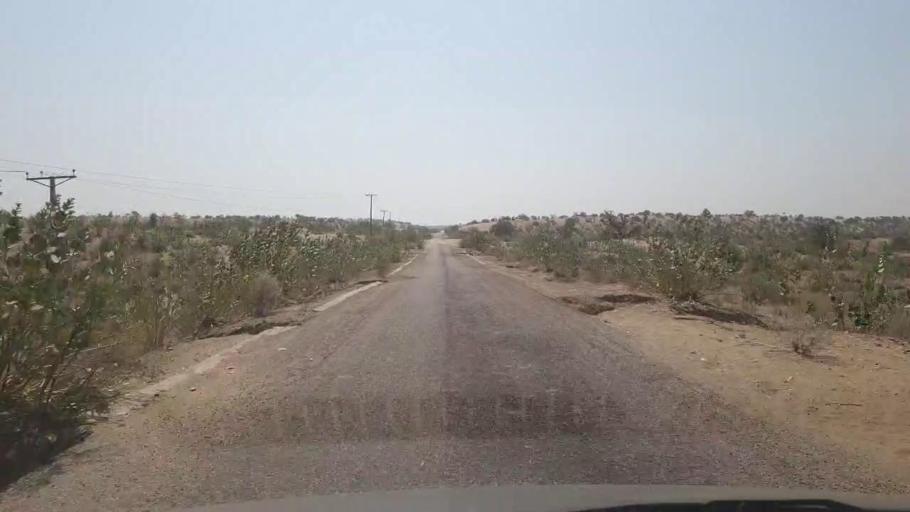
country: PK
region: Sindh
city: Chor
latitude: 25.6607
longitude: 70.1670
